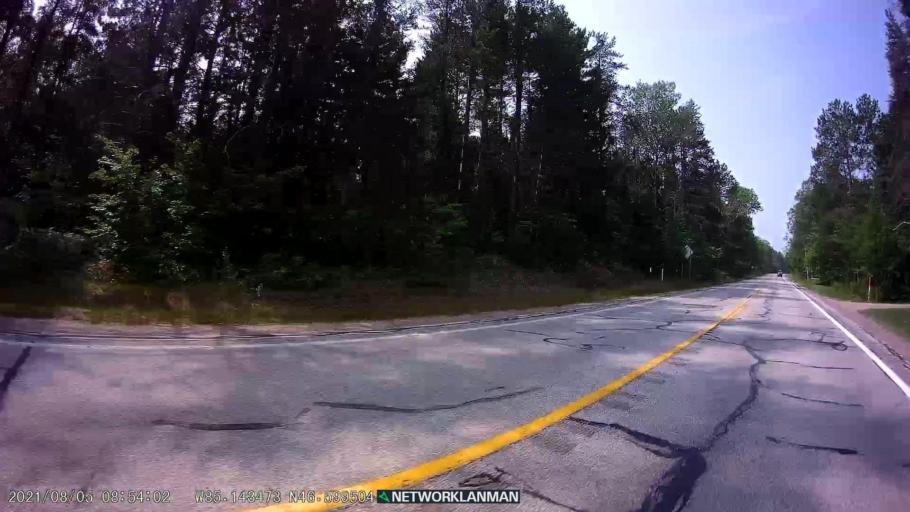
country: US
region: Michigan
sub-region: Luce County
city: Newberry
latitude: 46.5991
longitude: -85.1447
